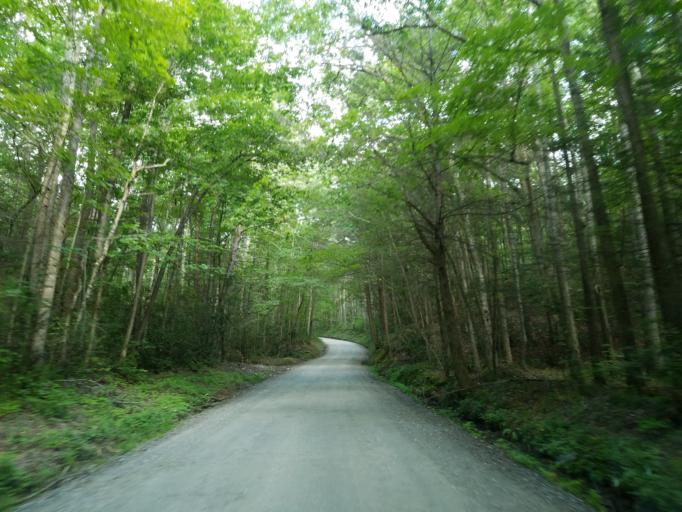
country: US
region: Georgia
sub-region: Fannin County
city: Blue Ridge
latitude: 34.7813
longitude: -84.3344
